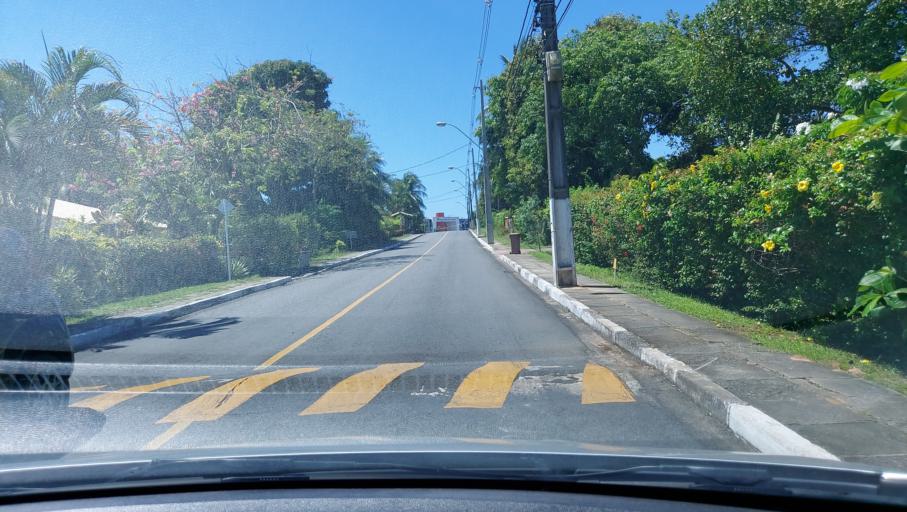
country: BR
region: Bahia
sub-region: Lauro De Freitas
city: Lauro de Freitas
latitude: -12.8719
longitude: -38.3065
